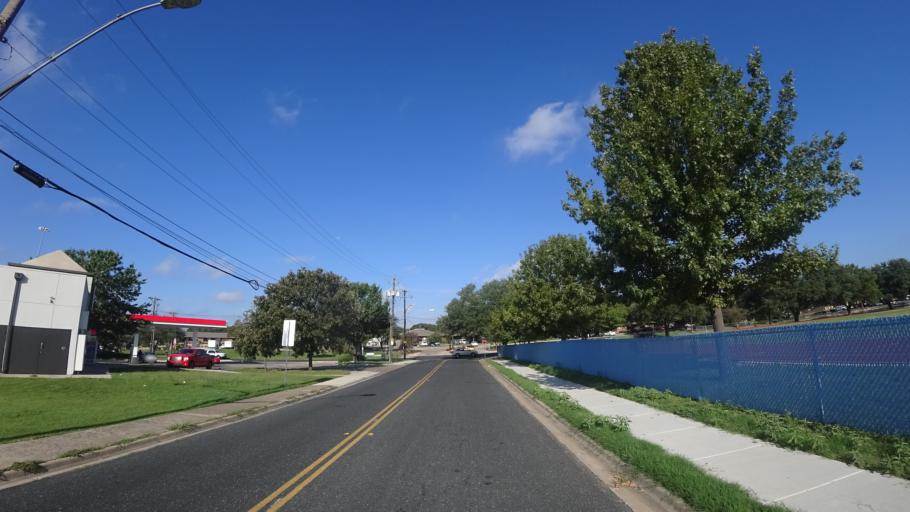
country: US
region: Texas
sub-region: Travis County
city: Austin
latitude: 30.3226
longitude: -97.6935
